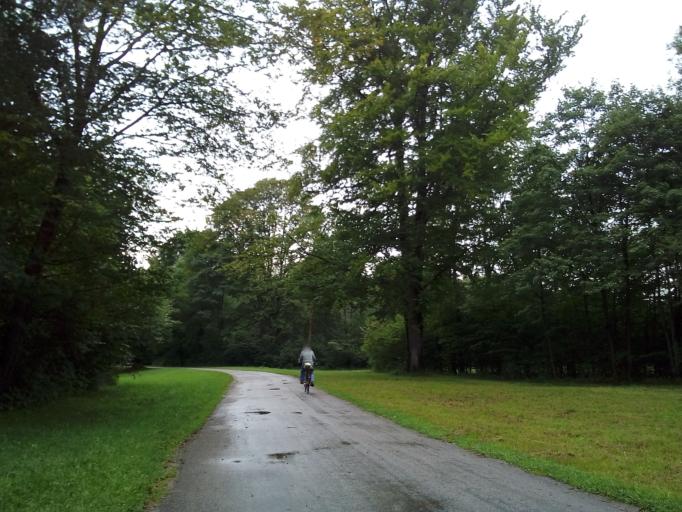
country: DE
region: Bavaria
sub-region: Upper Bavaria
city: Bogenhausen
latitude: 48.1754
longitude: 11.6146
